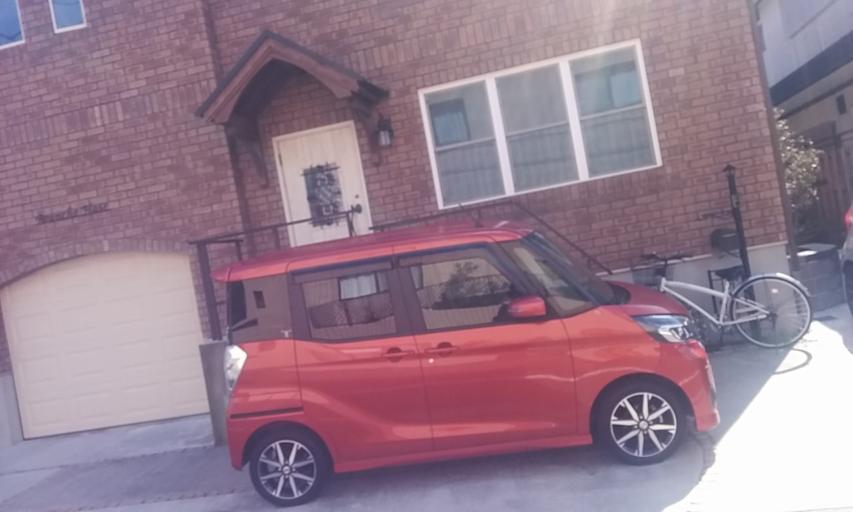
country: JP
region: Kanagawa
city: Kamakura
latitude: 35.3185
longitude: 139.5379
